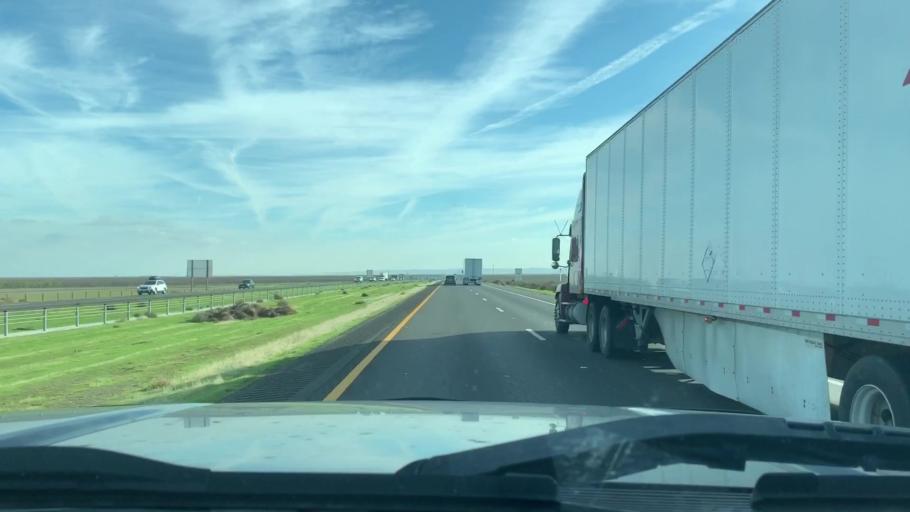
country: US
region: California
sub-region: Fresno County
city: Huron
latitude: 36.2466
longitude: -120.2393
